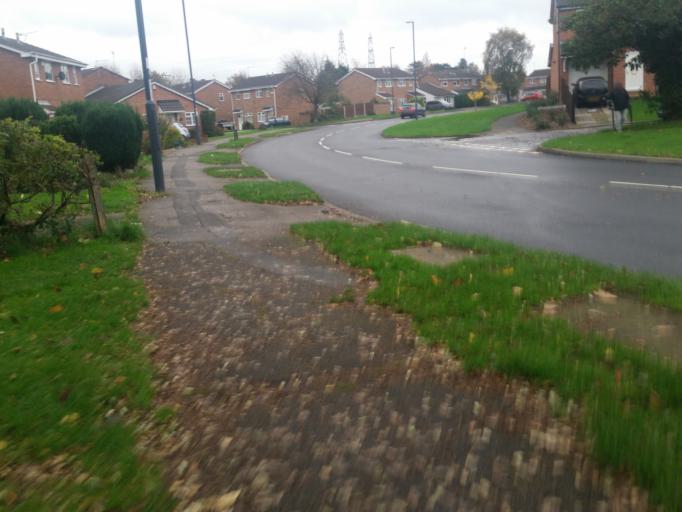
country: GB
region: England
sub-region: Derbyshire
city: Borrowash
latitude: 52.8915
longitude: -1.4123
